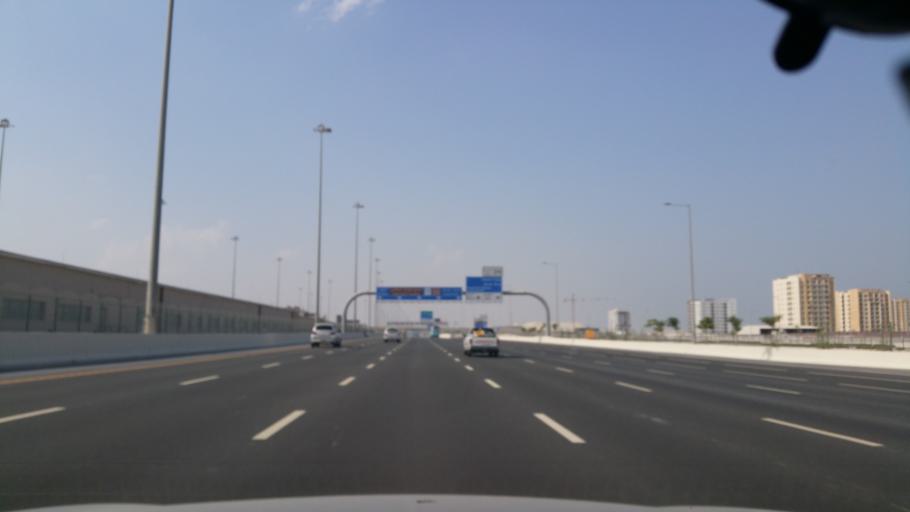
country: QA
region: Baladiyat Umm Salal
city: Umm Salal Muhammad
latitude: 25.4202
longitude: 51.4870
